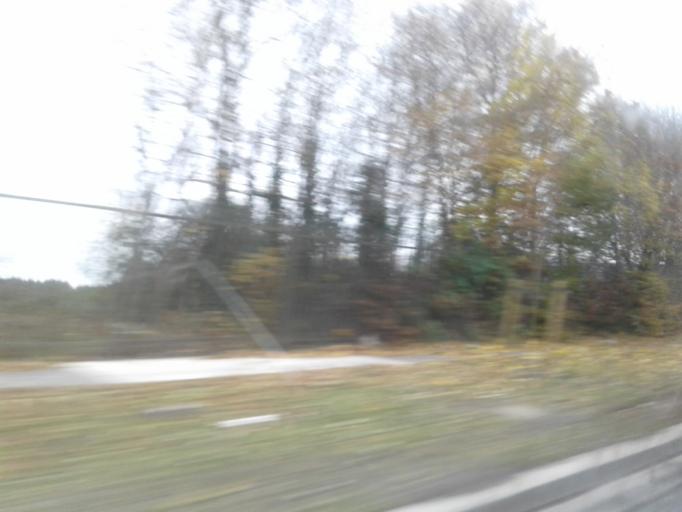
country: IE
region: Leinster
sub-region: Fingal County
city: Blanchardstown
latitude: 53.4069
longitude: -6.3661
